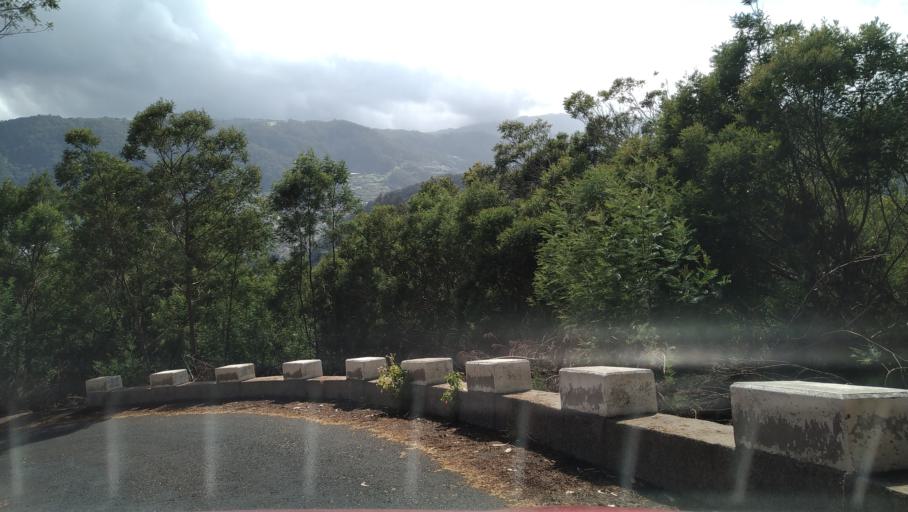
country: PT
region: Madeira
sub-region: Machico
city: Canical
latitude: 32.7419
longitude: -16.7710
